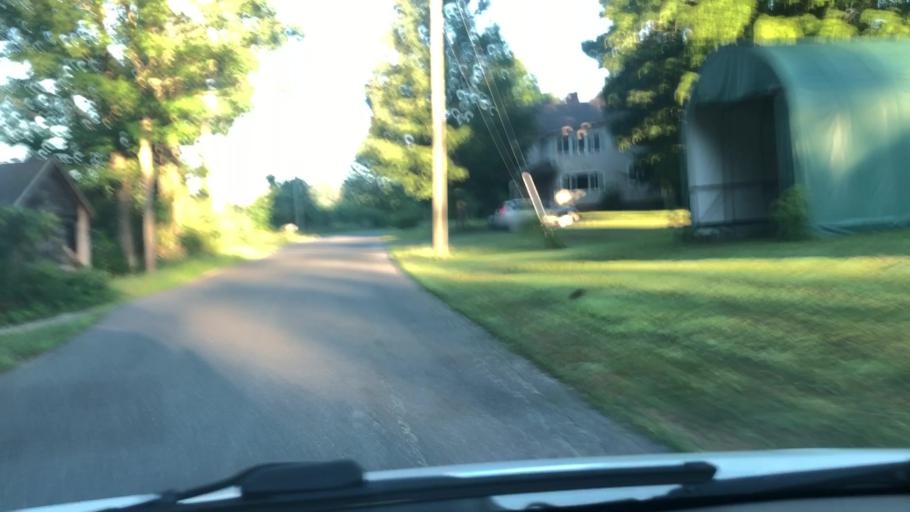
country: US
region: Massachusetts
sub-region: Hampshire County
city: Southampton
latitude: 42.2453
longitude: -72.7074
